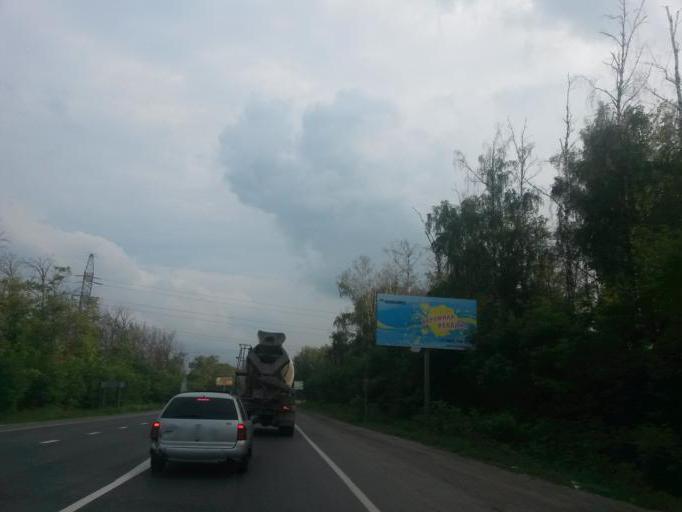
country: RU
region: Moskovskaya
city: Petrovskaya
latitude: 55.5363
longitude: 37.7695
